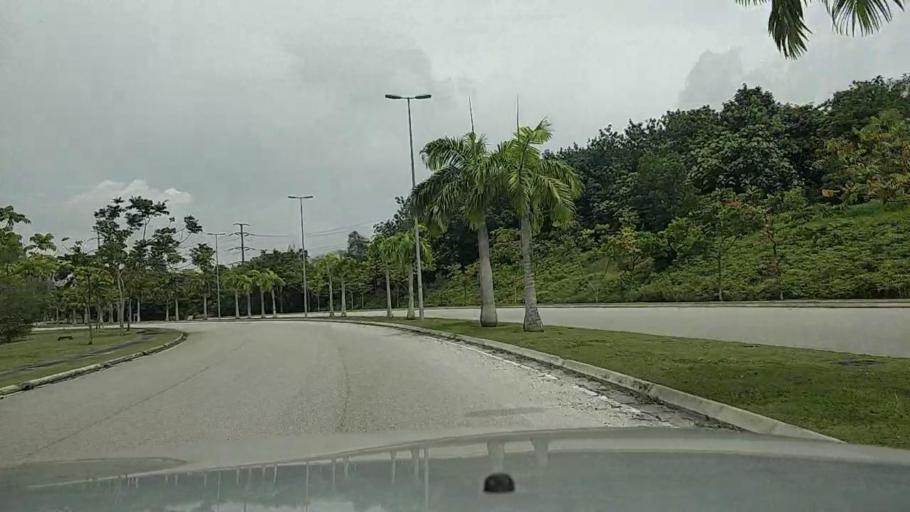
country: MY
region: Putrajaya
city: Putrajaya
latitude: 2.9022
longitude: 101.6518
